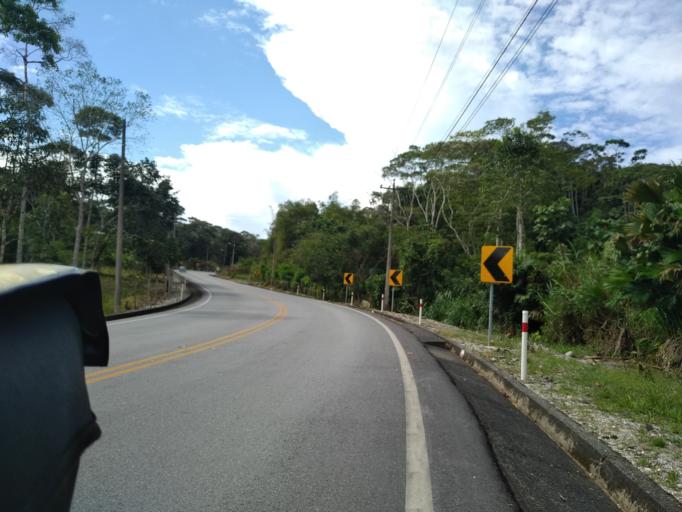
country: EC
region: Napo
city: Tena
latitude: -1.0960
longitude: -77.7941
